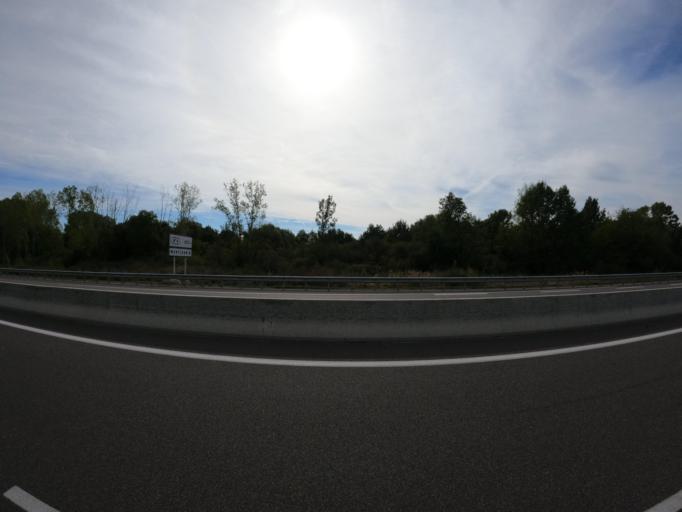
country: FR
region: Bourgogne
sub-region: Departement de Saone-et-Loire
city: Saint-Eusebe
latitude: 46.7304
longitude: 4.4662
